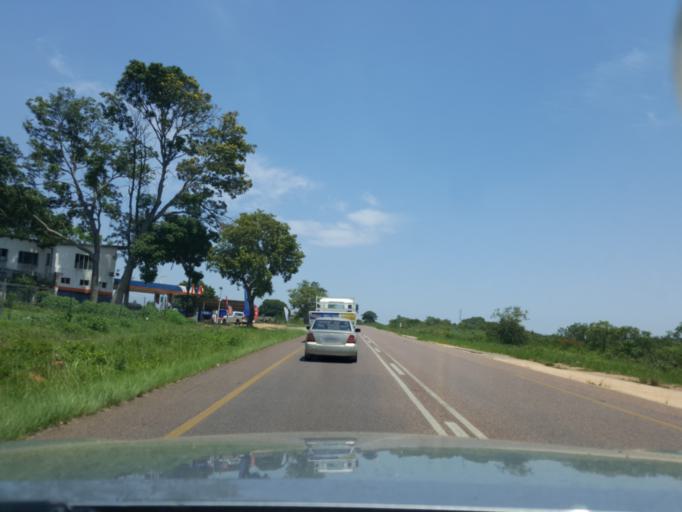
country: ZA
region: Limpopo
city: Thulamahashi
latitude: -24.8938
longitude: 31.1054
